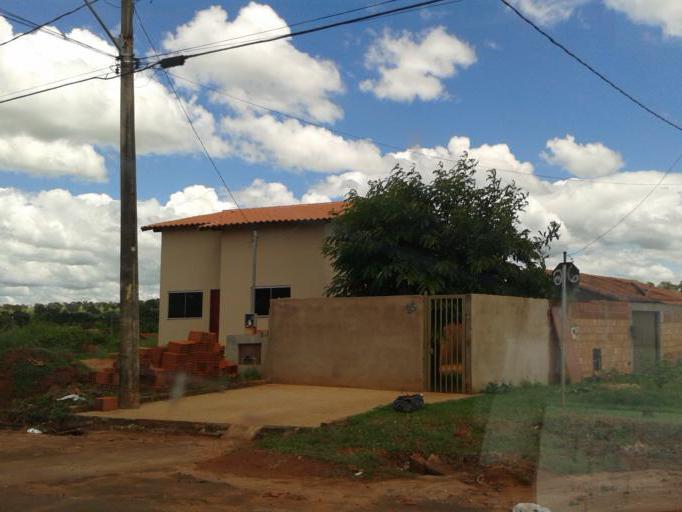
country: BR
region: Minas Gerais
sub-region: Santa Vitoria
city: Santa Vitoria
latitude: -18.8471
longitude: -50.1336
